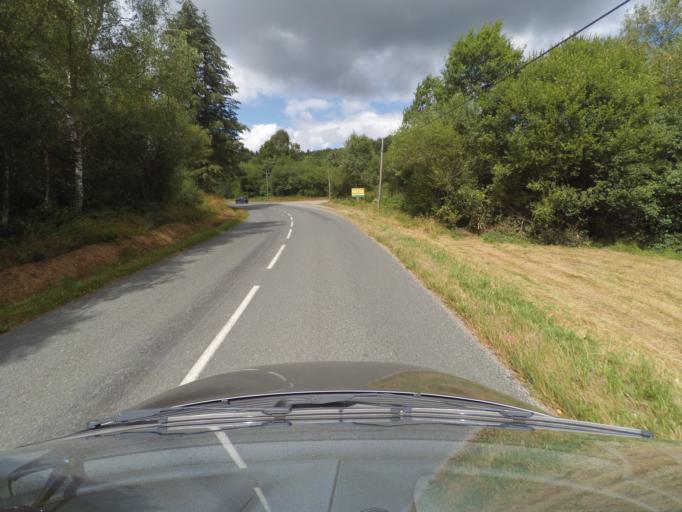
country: FR
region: Limousin
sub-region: Departement de la Haute-Vienne
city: Peyrat-le-Chateau
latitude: 45.8955
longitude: 1.8796
